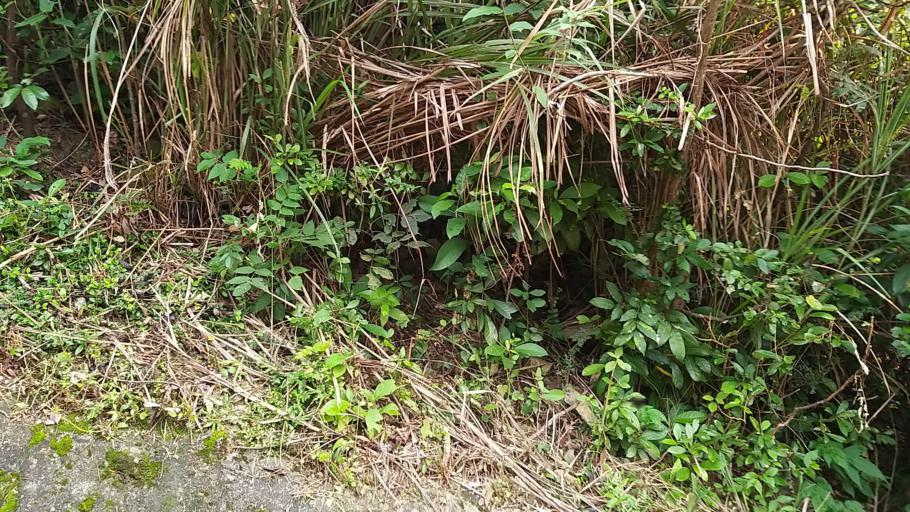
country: HK
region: Tuen Mun
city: Tuen Mun
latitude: 22.4037
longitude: 113.9828
